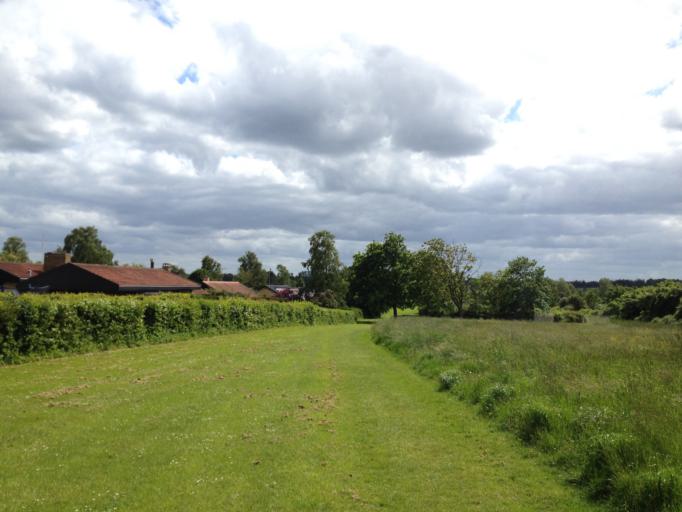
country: DK
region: Capital Region
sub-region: Fredensborg Kommune
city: Niva
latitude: 55.9357
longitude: 12.4869
